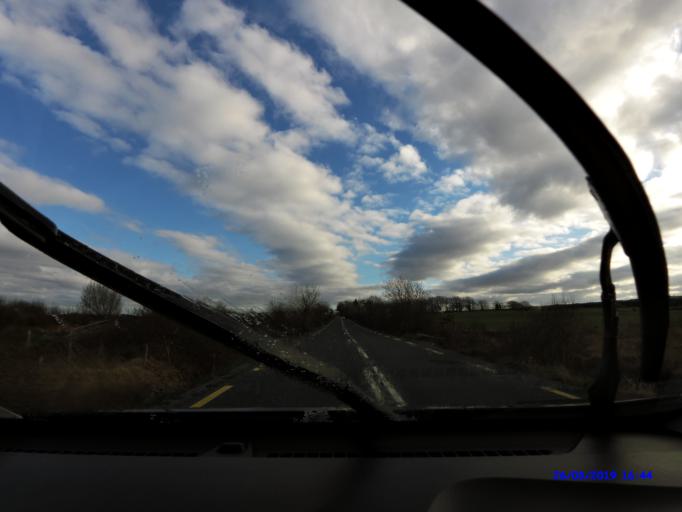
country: IE
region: Connaught
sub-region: Maigh Eo
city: Ballyhaunis
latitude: 53.8476
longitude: -8.7659
